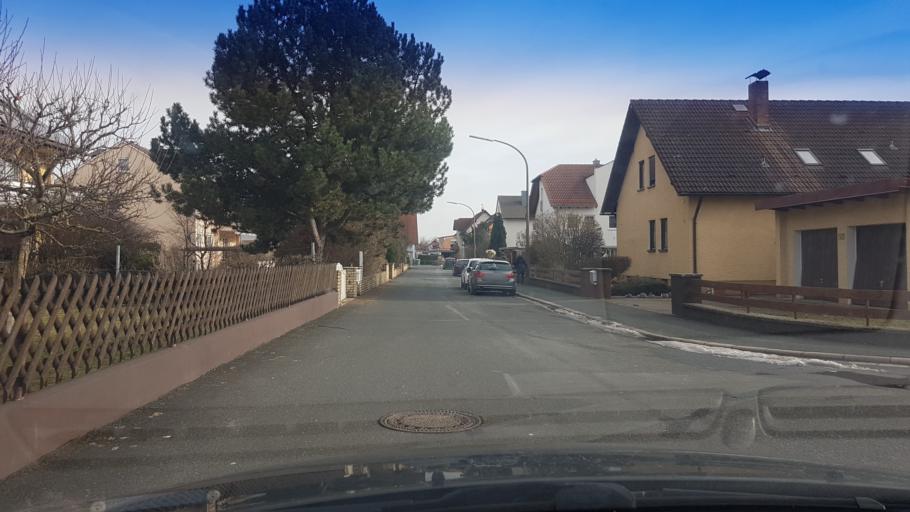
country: DE
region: Bavaria
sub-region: Upper Franconia
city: Hirschaid
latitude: 49.8234
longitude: 10.9921
